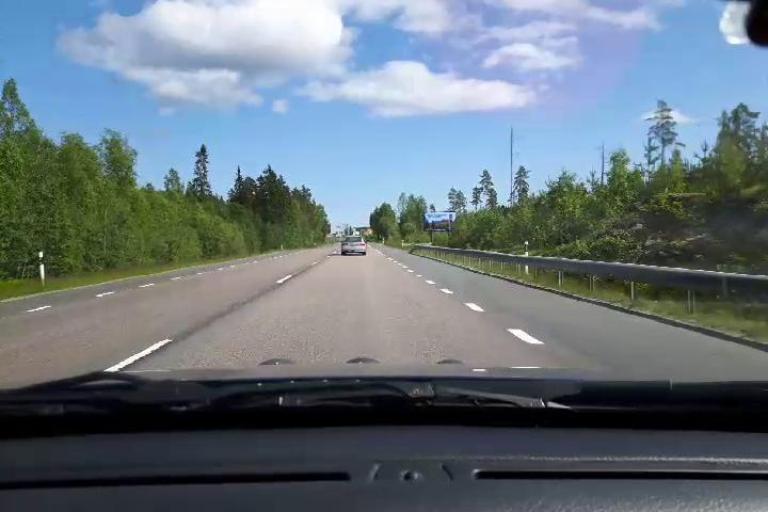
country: SE
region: Gaevleborg
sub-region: Hudiksvalls Kommun
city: Sorforsa
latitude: 61.7171
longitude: 17.0317
